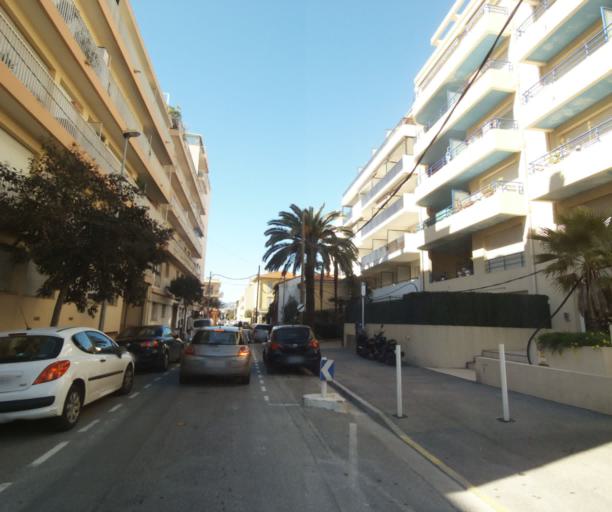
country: FR
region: Provence-Alpes-Cote d'Azur
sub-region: Departement des Alpes-Maritimes
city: Antibes
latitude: 43.5716
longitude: 7.1034
